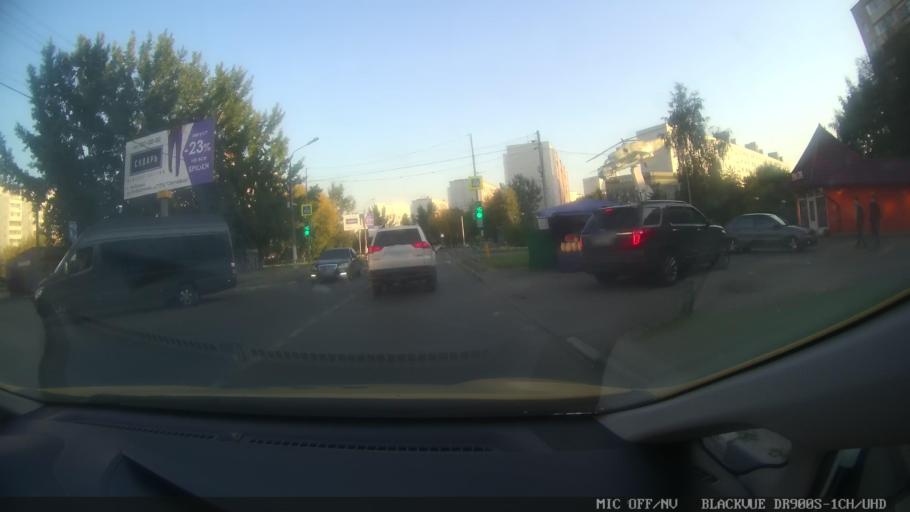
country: RU
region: Moscow
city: Nekrasovka
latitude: 55.6960
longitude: 37.9012
